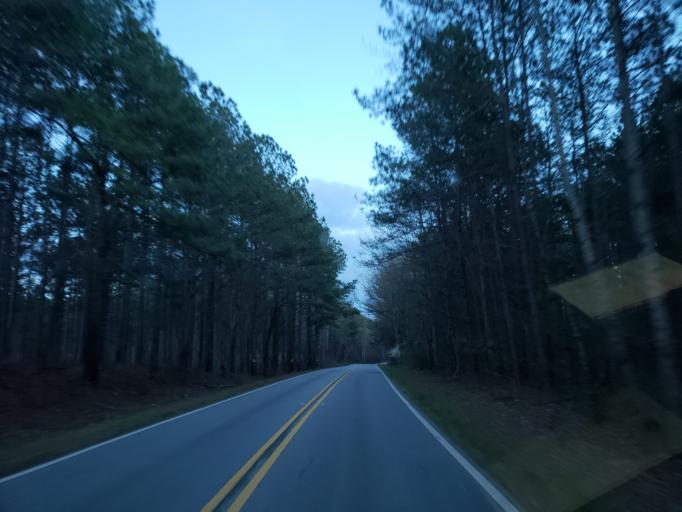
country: US
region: Georgia
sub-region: Polk County
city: Rockmart
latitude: 33.9900
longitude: -84.9455
